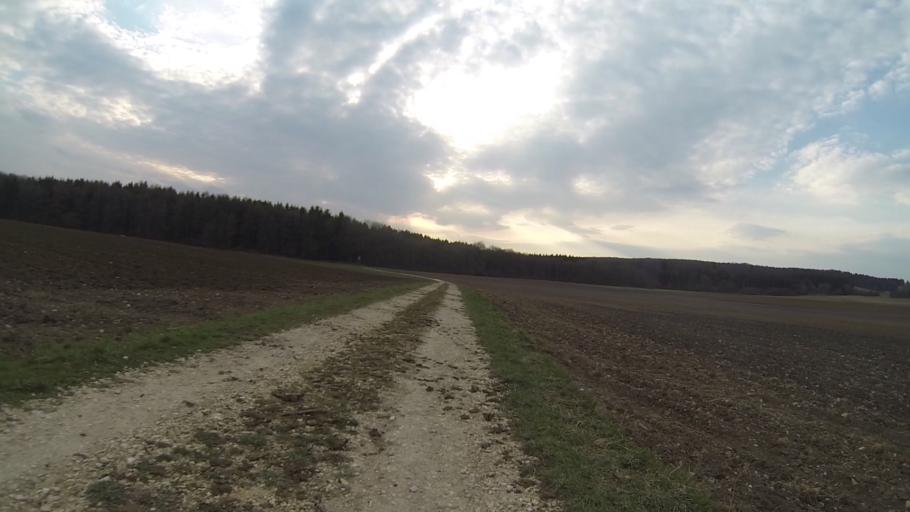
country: DE
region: Baden-Wuerttemberg
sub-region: Regierungsbezirk Stuttgart
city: Bolheim
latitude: 48.6230
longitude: 10.1314
